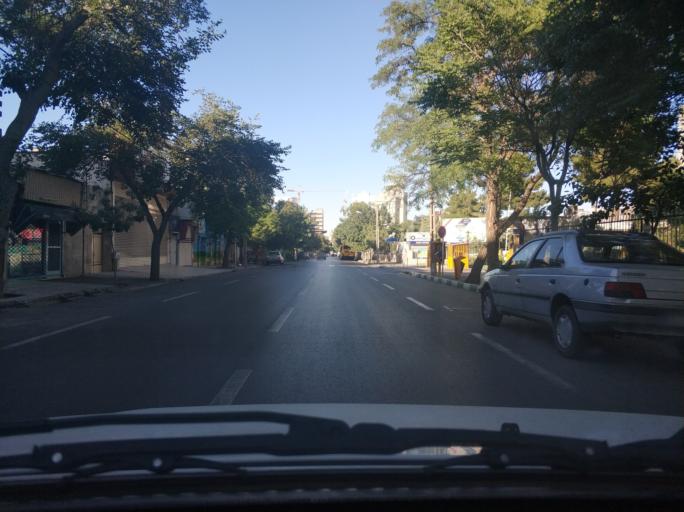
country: IR
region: Razavi Khorasan
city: Mashhad
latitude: 36.2781
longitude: 59.5949
